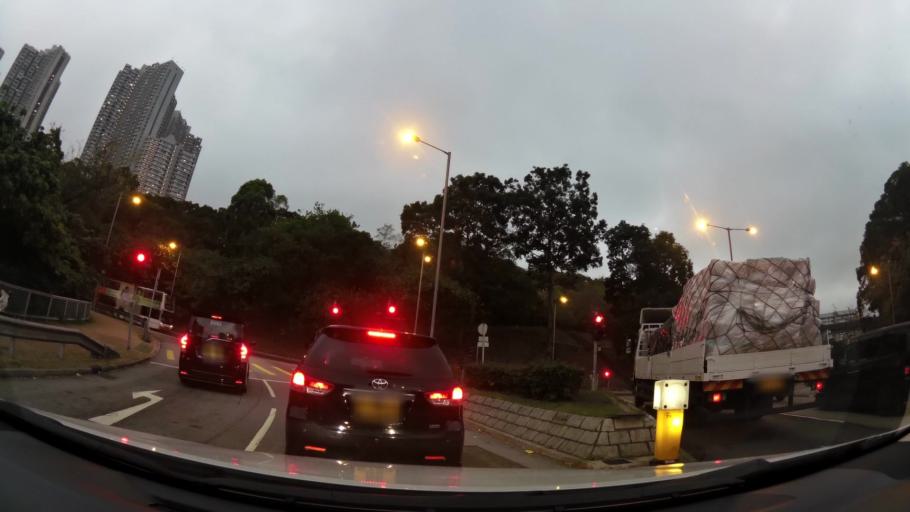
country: HK
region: Tsuen Wan
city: Tsuen Wan
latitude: 22.3574
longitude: 114.1016
